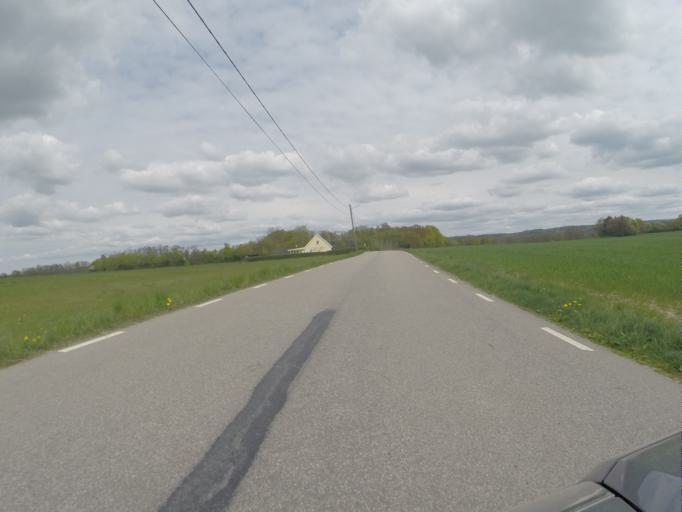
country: SE
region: Skane
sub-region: Bjuvs Kommun
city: Bjuv
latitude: 56.0747
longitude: 12.9564
